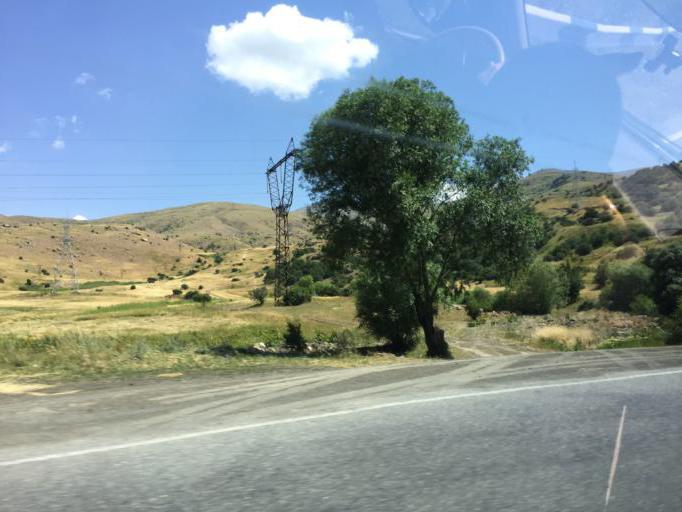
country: AM
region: Vayots' Dzori Marz
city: Jermuk
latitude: 39.7131
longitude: 45.6666
